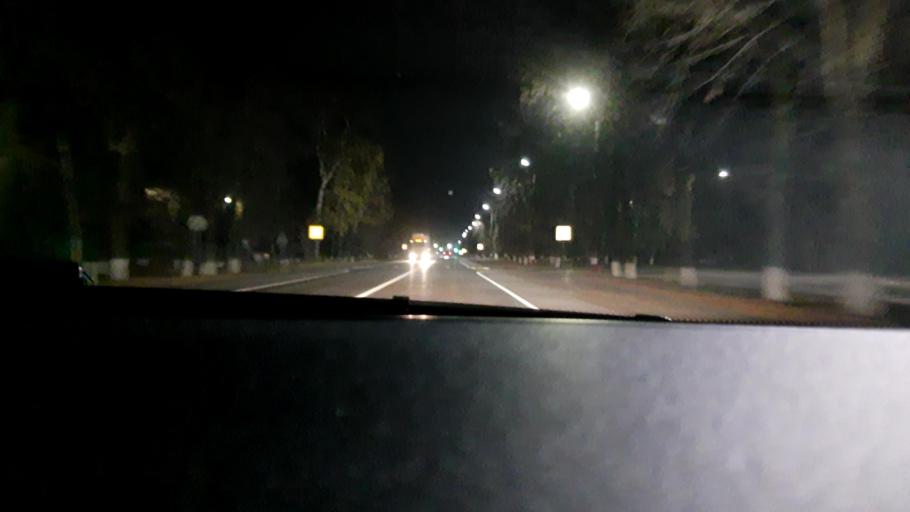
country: RU
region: Nizjnij Novgorod
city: Gidrotorf
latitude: 56.5245
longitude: 43.5598
